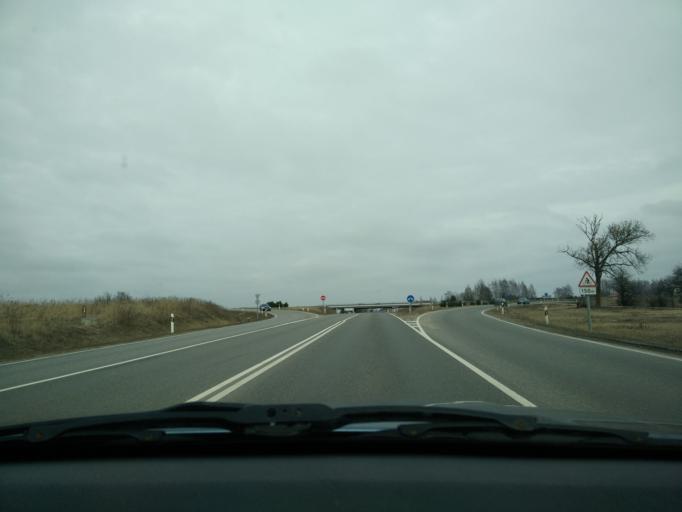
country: LT
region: Klaipedos apskritis
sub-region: Klaipeda
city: Klaipeda
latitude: 55.7299
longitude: 21.1809
